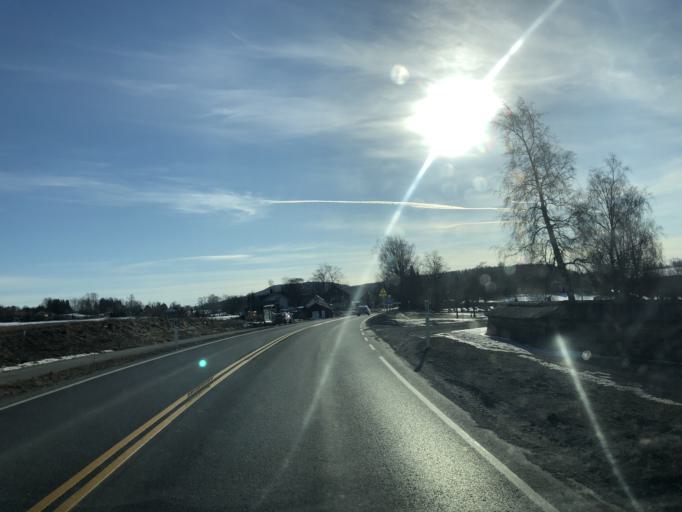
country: NO
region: Hedmark
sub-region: Ringsaker
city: Moelv
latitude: 60.9035
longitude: 10.7245
